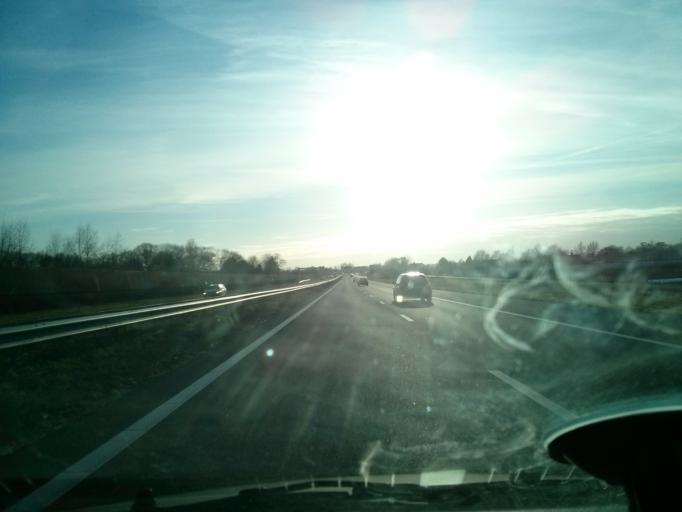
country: NL
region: North Brabant
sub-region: Gemeente Veghel
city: Mariaheide
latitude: 51.6433
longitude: 5.5845
